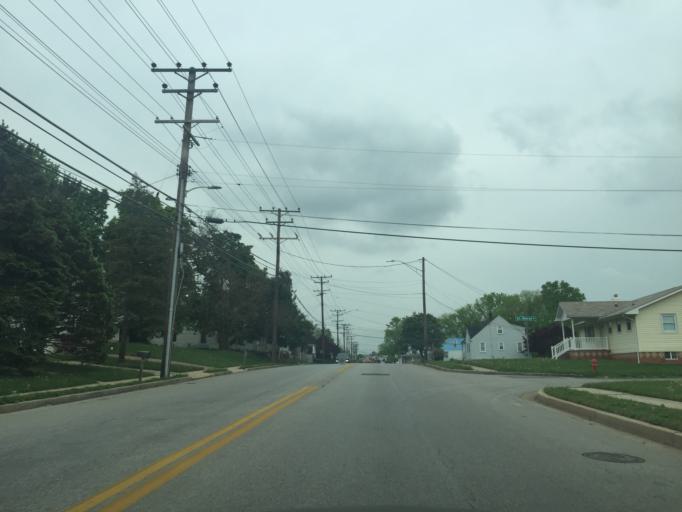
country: US
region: Maryland
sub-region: Baltimore County
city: Catonsville
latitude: 39.2957
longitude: -76.7272
